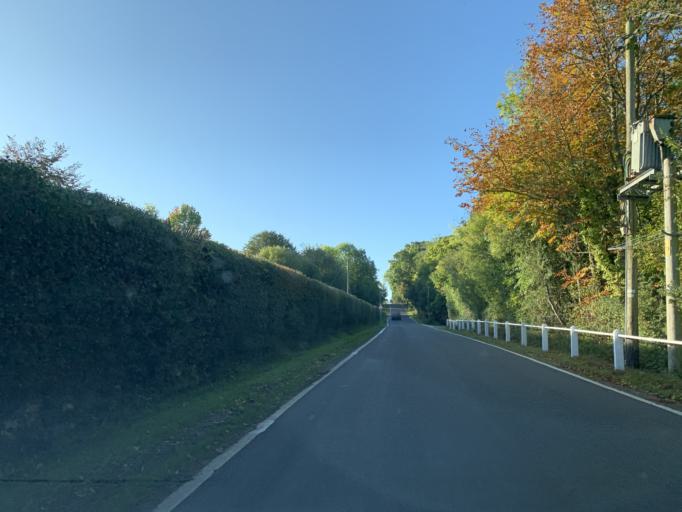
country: GB
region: England
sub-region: Hampshire
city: Cadnam
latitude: 50.9422
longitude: -1.6179
